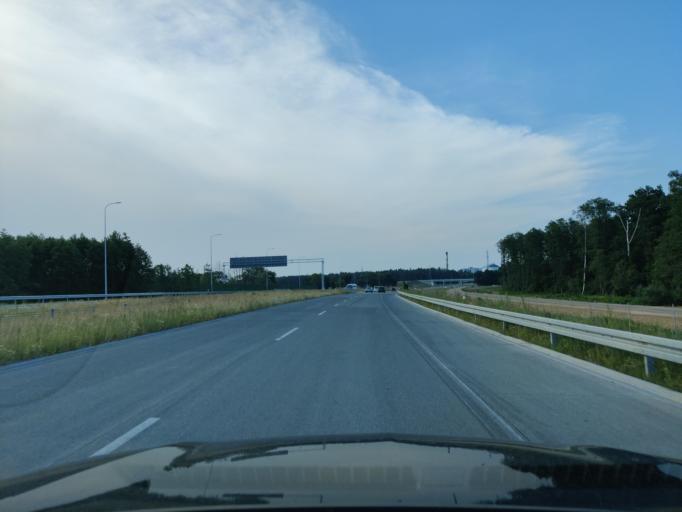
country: PL
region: Masovian Voivodeship
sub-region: Powiat ciechanowski
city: Glinojeck
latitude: 52.8257
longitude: 20.2615
